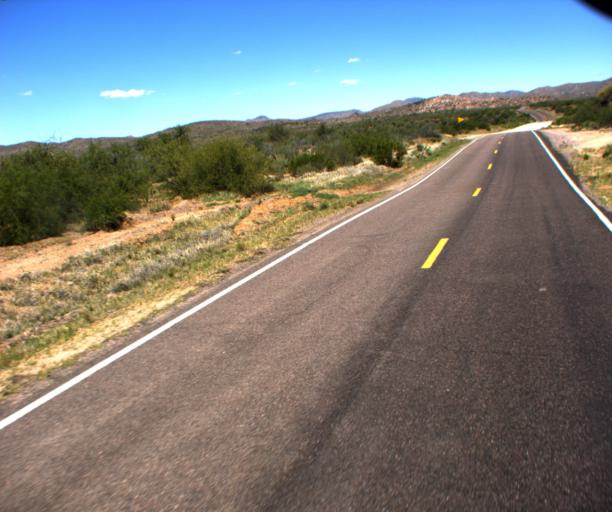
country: US
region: Arizona
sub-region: Yavapai County
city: Bagdad
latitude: 34.5103
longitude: -113.1512
